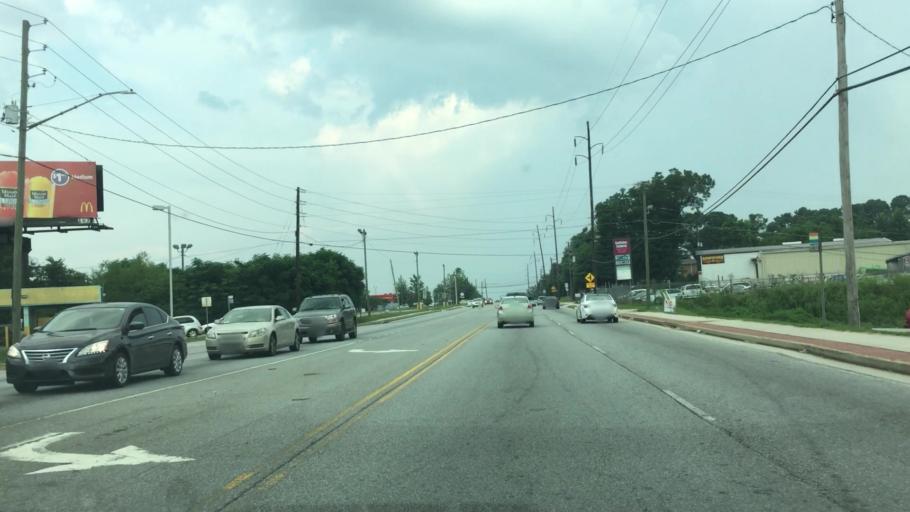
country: US
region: Georgia
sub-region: DeKalb County
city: Belvedere Park
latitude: 33.7591
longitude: -84.2408
